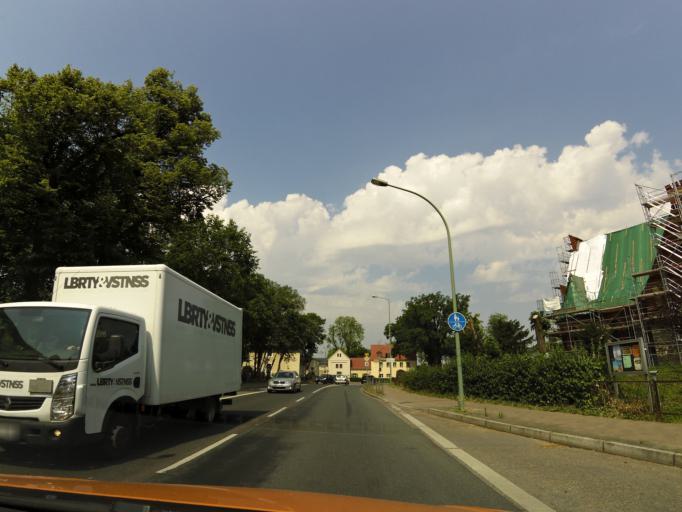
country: DE
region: Brandenburg
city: Potsdam
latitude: 52.4233
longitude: 13.0003
